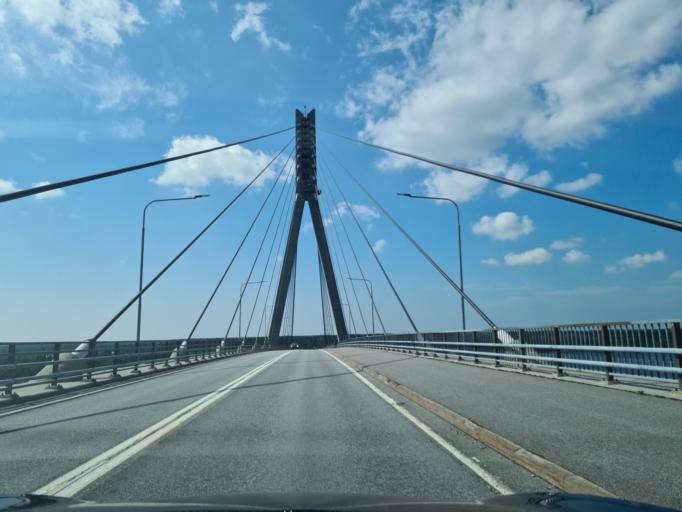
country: FI
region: Ostrobothnia
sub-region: Vaasa
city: Replot
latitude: 63.2069
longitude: 21.4740
